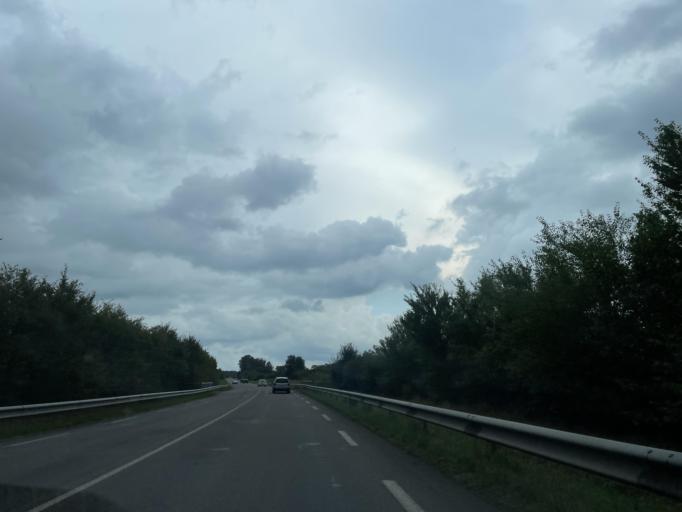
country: FR
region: Haute-Normandie
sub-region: Departement de la Seine-Maritime
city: Forges-les-Eaux
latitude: 49.6013
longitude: 1.5220
